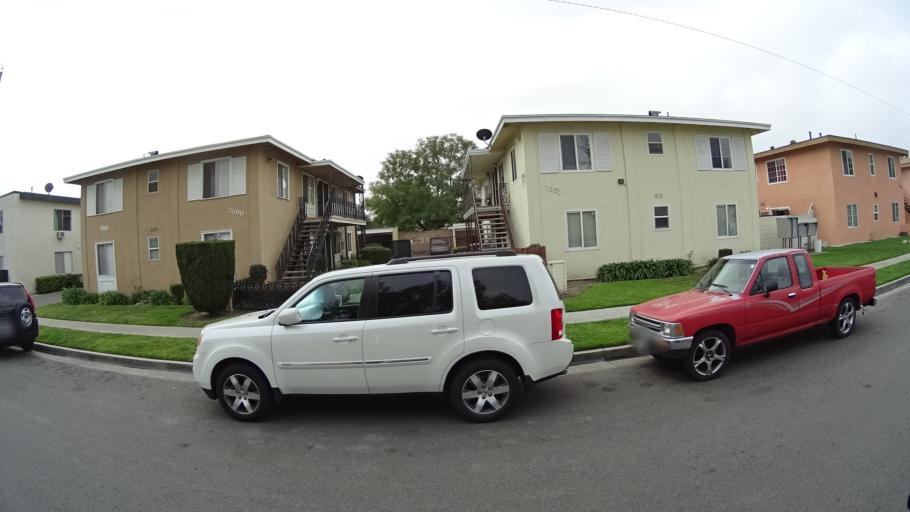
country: US
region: California
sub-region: Orange County
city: Buena Park
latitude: 33.8361
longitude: -118.0009
